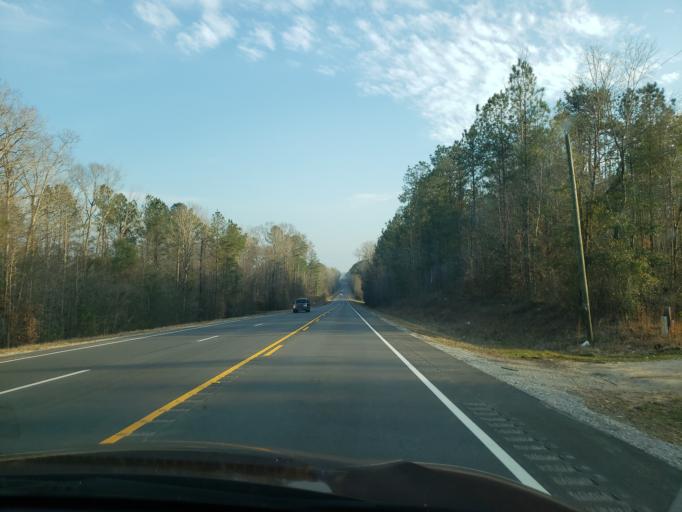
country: US
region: Alabama
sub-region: Hale County
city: Greensboro
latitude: 32.8511
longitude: -87.6119
